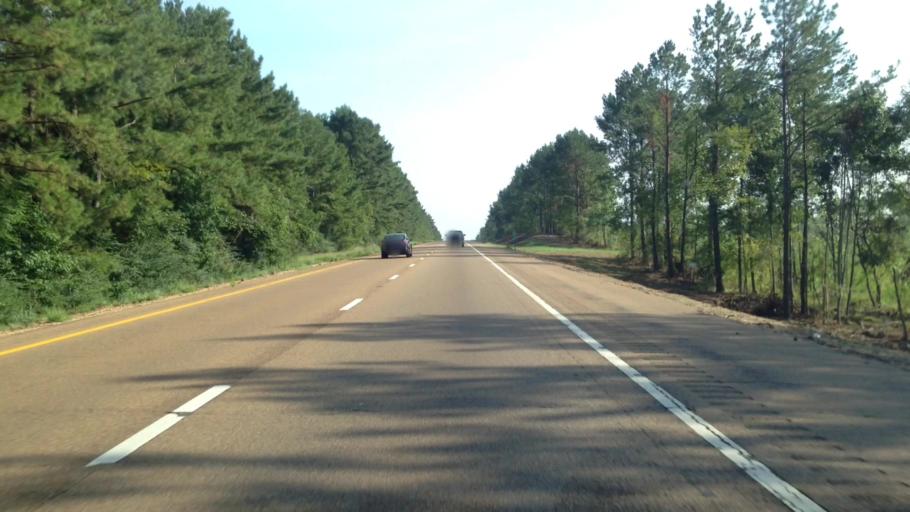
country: US
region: Mississippi
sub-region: Lincoln County
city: Brookhaven
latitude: 31.4618
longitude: -90.4788
